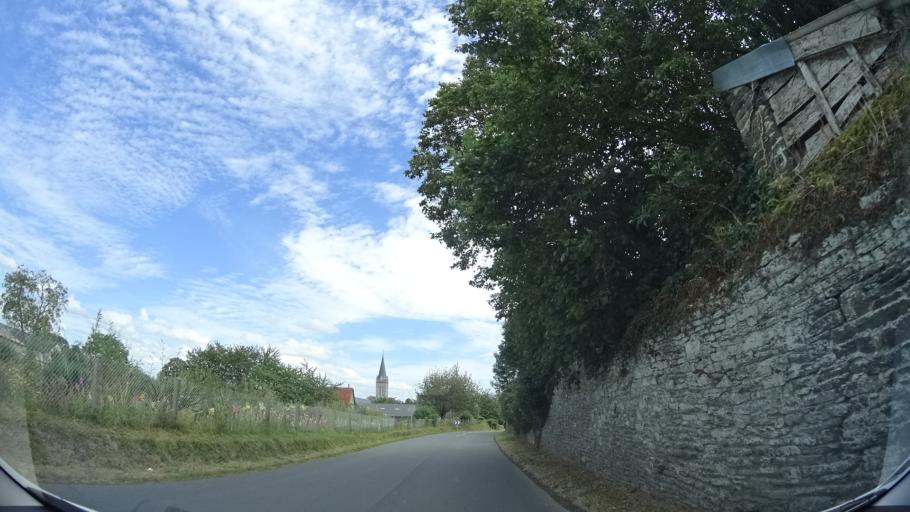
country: FR
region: Lower Normandy
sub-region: Departement de la Manche
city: Marcey-les-Greves
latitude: 48.6823
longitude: -1.4144
